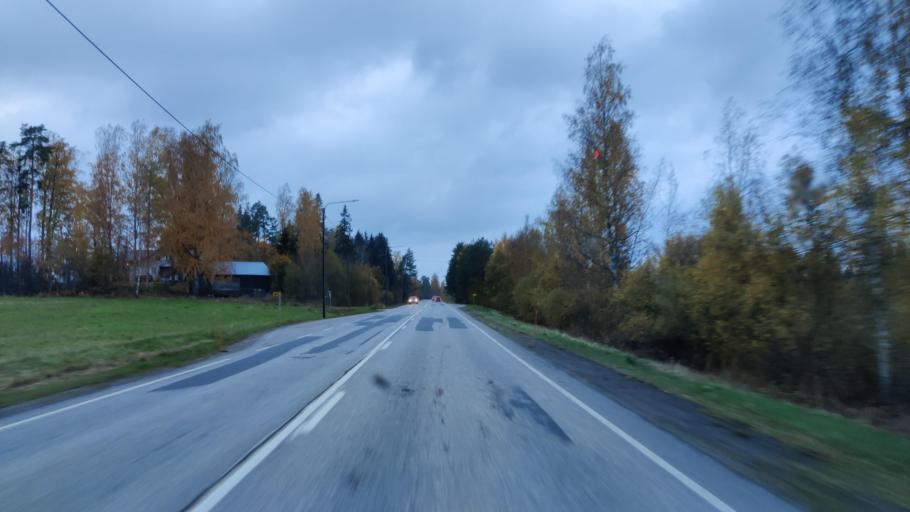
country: FI
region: Uusimaa
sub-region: Helsinki
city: Vihti
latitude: 60.3370
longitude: 24.1987
